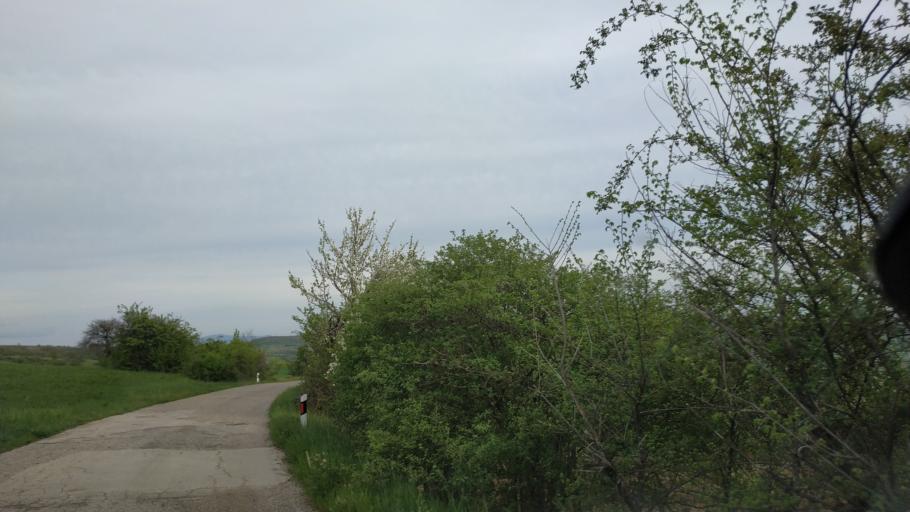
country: RS
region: Central Serbia
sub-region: Zajecarski Okrug
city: Soko Banja
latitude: 43.5329
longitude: 21.8765
